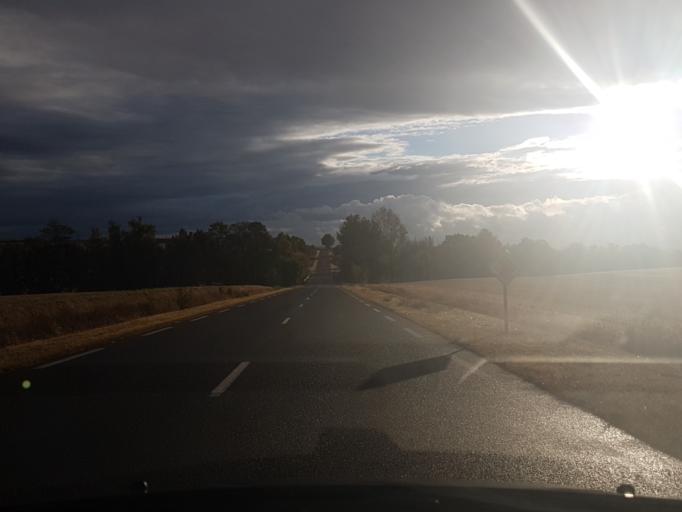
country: FR
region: Languedoc-Roussillon
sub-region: Departement de l'Aude
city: Bram
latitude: 43.1758
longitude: 2.0142
